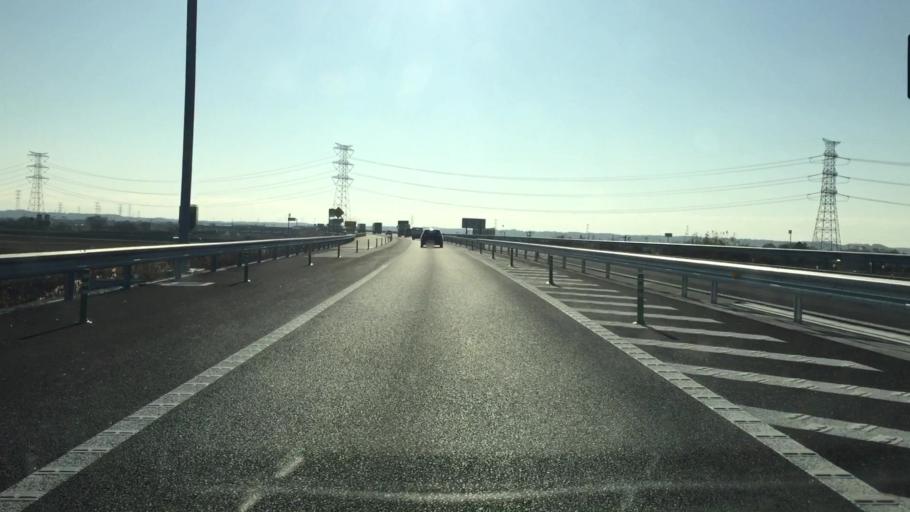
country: JP
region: Ibaraki
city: Edosaki
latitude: 35.9199
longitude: 140.3506
